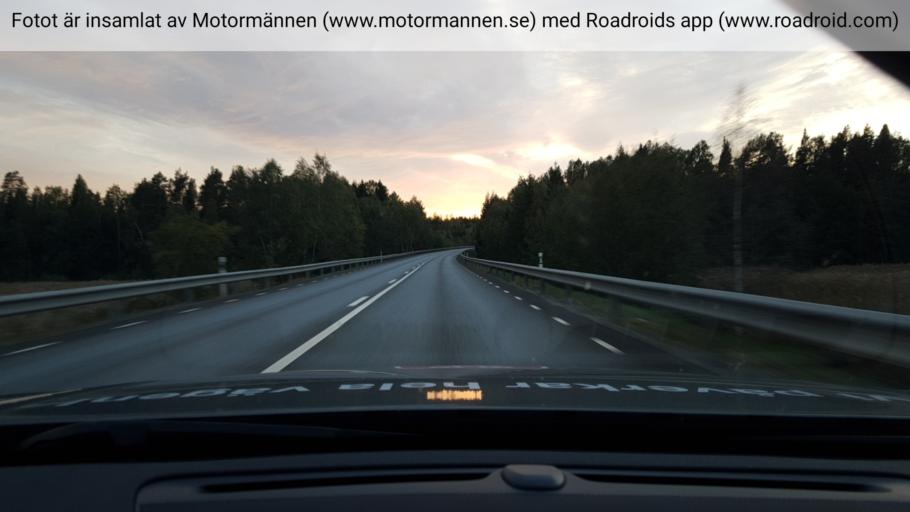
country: SE
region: Vaermland
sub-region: Saffle Kommun
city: Saeffle
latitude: 59.2477
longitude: 12.8209
